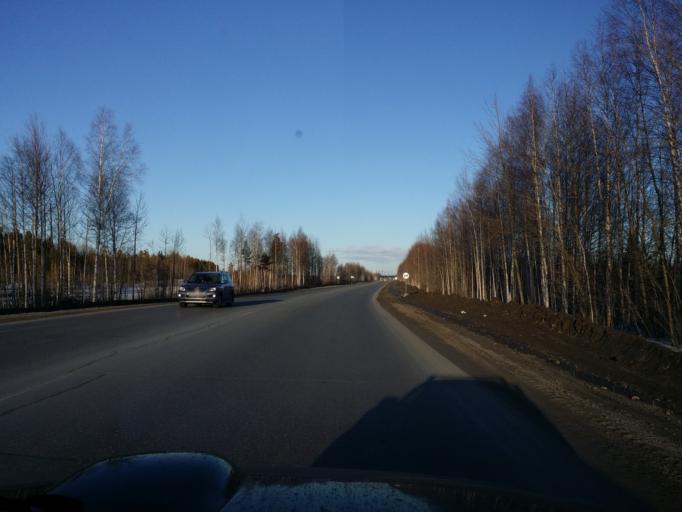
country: RU
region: Khanty-Mansiyskiy Avtonomnyy Okrug
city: Megion
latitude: 61.0679
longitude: 76.2212
